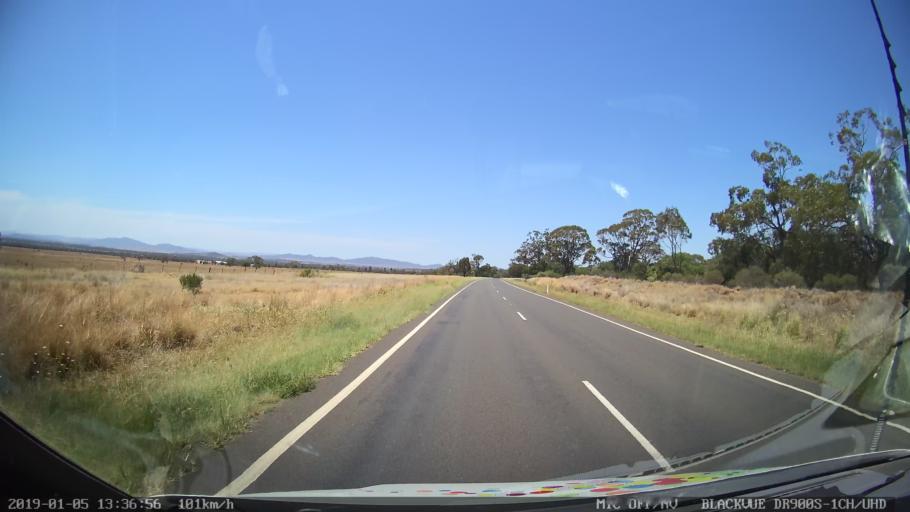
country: AU
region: New South Wales
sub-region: Gunnedah
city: Gunnedah
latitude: -30.9826
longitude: 150.1729
